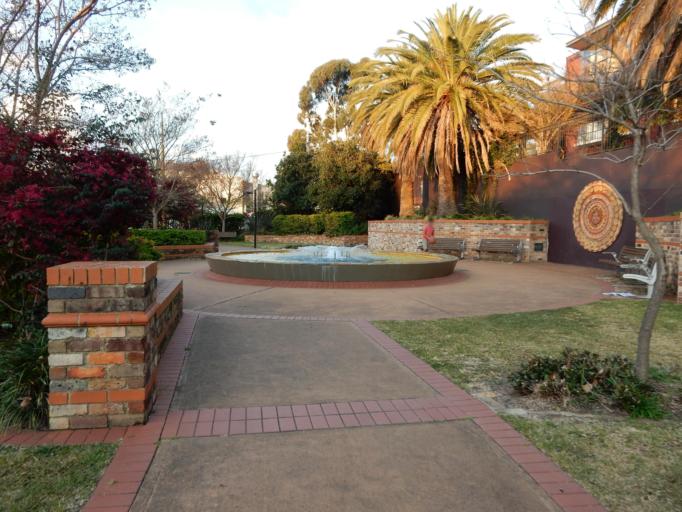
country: AU
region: New South Wales
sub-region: Willoughby
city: Chatswood
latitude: -33.7940
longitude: 151.1911
